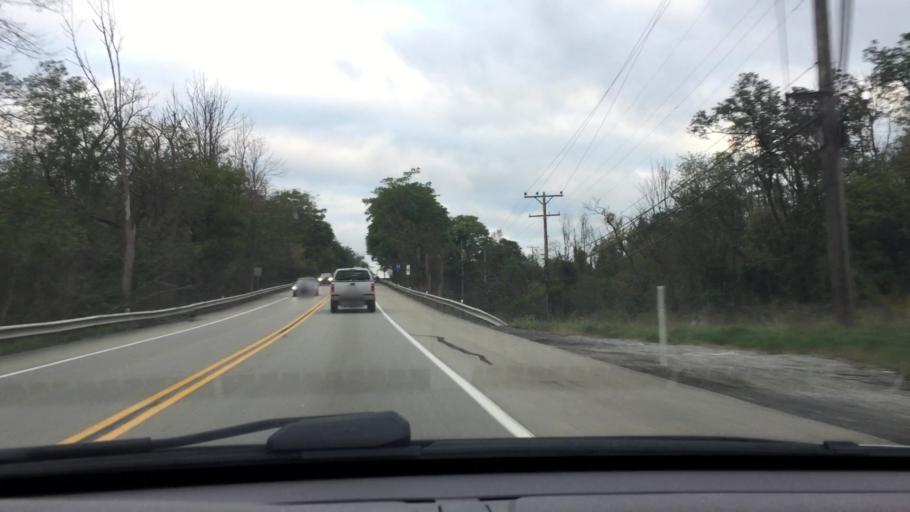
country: US
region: Pennsylvania
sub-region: Washington County
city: Canonsburg
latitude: 40.2381
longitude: -80.1746
